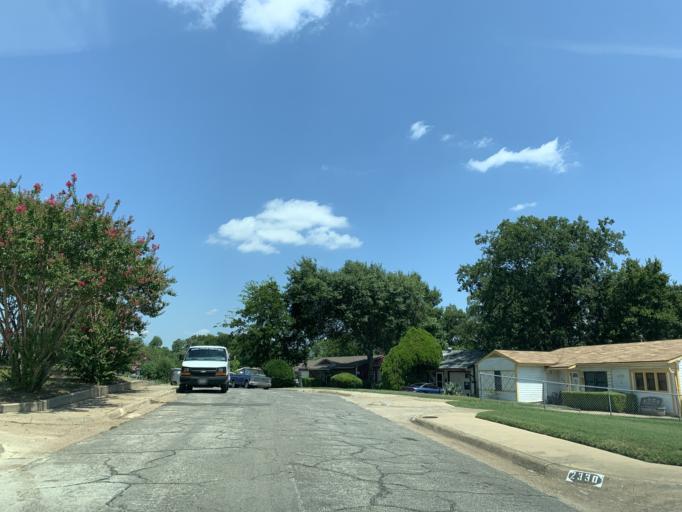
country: US
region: Texas
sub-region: Dallas County
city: Hutchins
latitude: 32.6830
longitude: -96.7816
